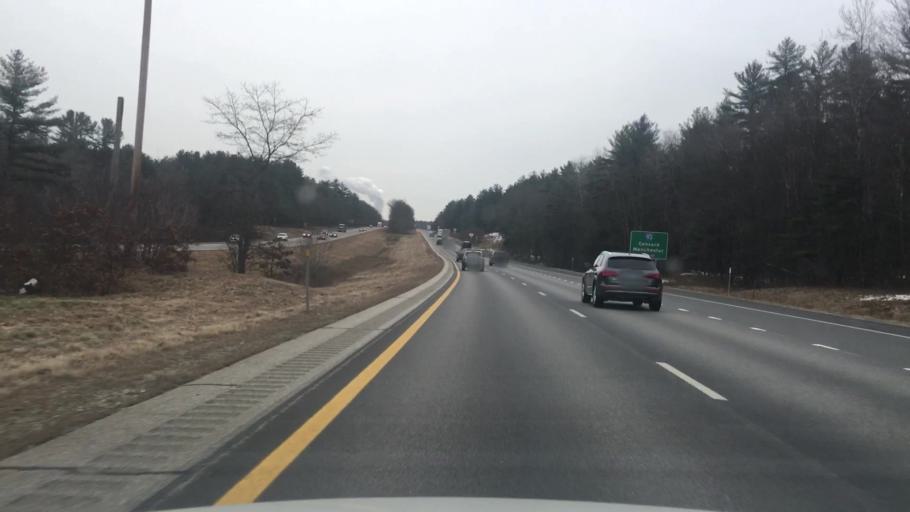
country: US
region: New Hampshire
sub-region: Merrimack County
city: Concord
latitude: 43.1771
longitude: -71.5617
